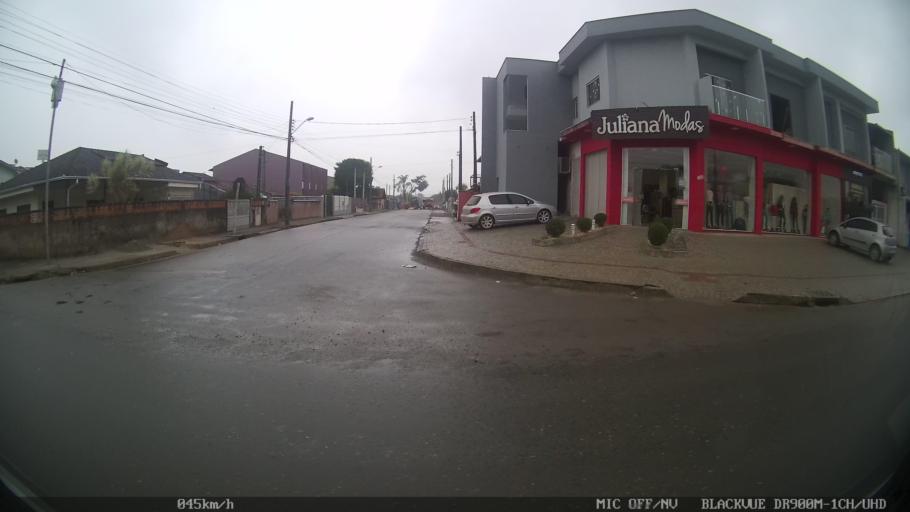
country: BR
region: Santa Catarina
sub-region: Joinville
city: Joinville
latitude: -26.2080
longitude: -48.8285
